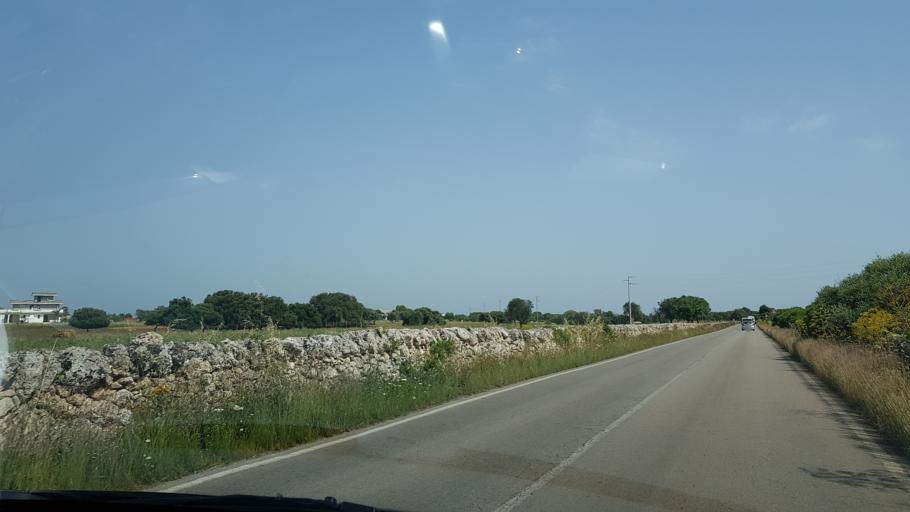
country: IT
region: Apulia
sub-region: Provincia di Lecce
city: Porto Cesareo
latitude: 40.3199
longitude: 17.8584
